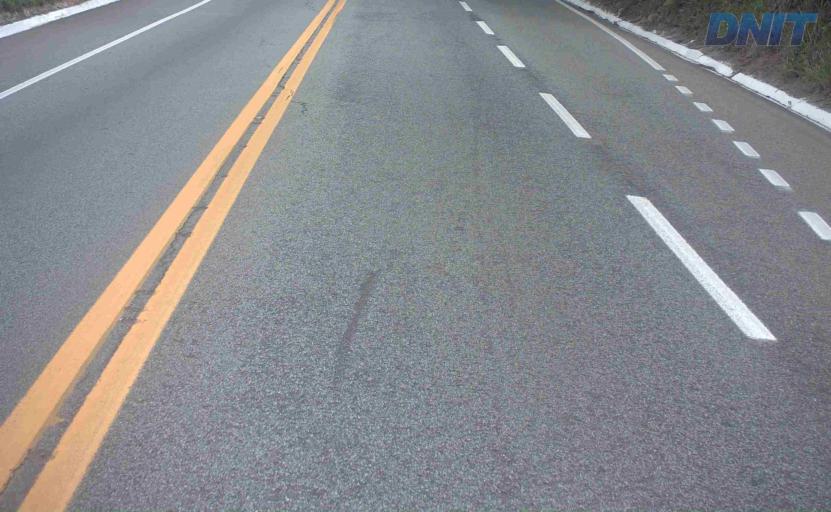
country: BR
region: Minas Gerais
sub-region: Santa Luzia
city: Santa Luzia
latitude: -19.7953
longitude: -43.7476
